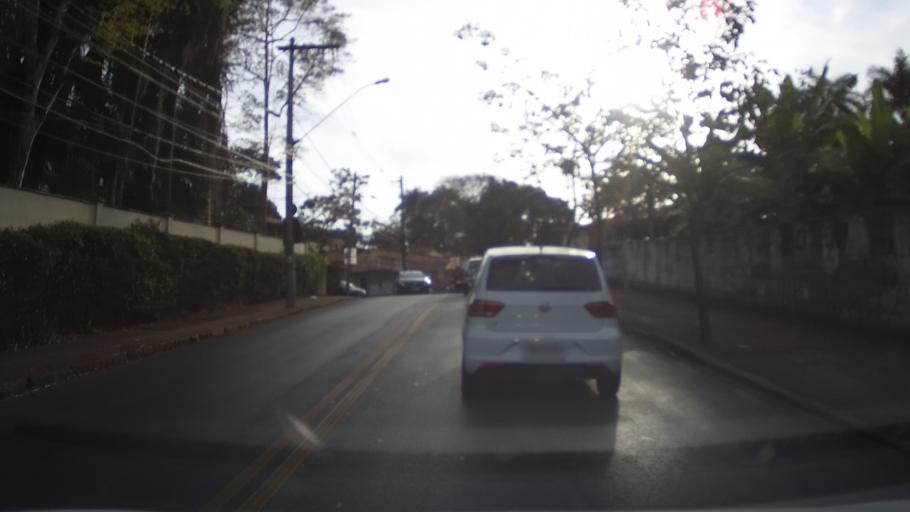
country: BR
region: Minas Gerais
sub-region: Belo Horizonte
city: Belo Horizonte
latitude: -19.8595
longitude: -43.9902
